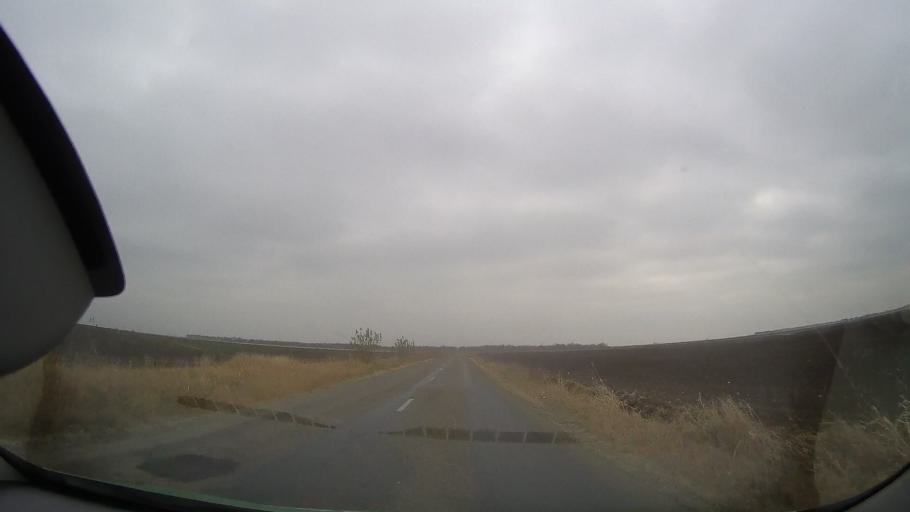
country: RO
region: Buzau
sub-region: Comuna Bradeanu
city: Bradeanu
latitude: 44.8939
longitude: 26.8735
